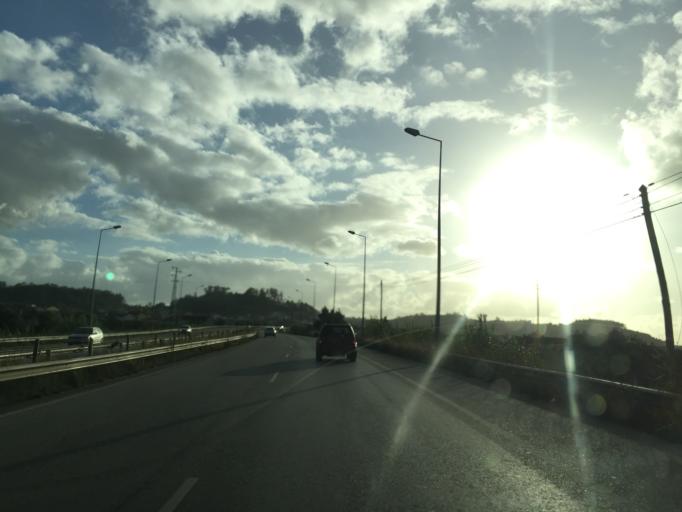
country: PT
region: Coimbra
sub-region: Coimbra
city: Coimbra
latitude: 40.2054
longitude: -8.4762
